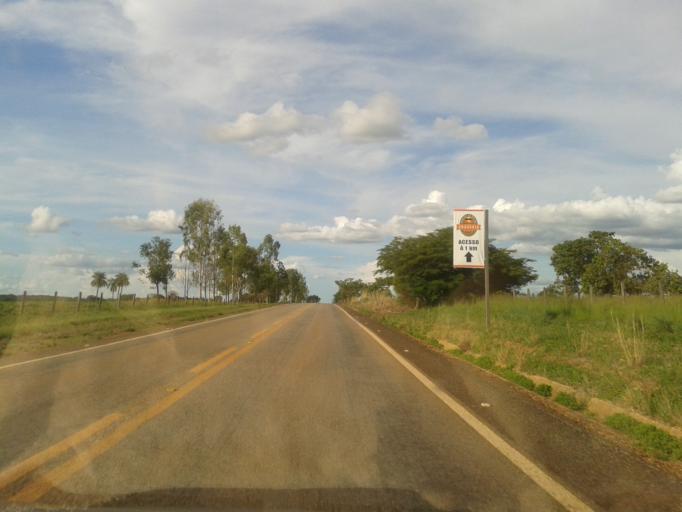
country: BR
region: Goias
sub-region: Crixas
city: Crixas
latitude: -14.2392
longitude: -50.3952
